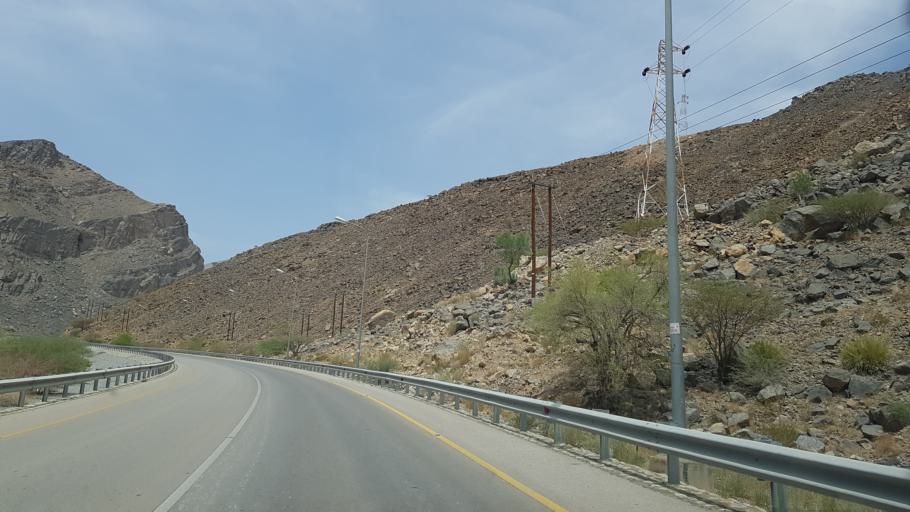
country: OM
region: Muhafazat ad Dakhiliyah
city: Izki
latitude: 22.9384
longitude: 57.6767
